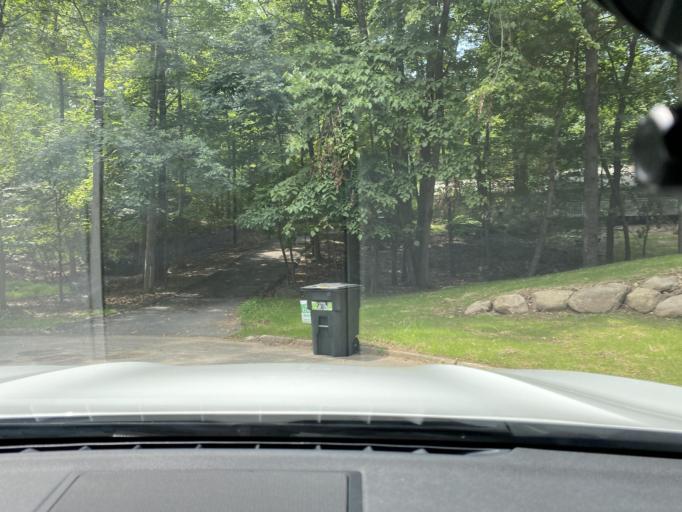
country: US
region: New Jersey
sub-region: Bergen County
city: Upper Saddle River
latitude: 41.0807
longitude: -74.1045
